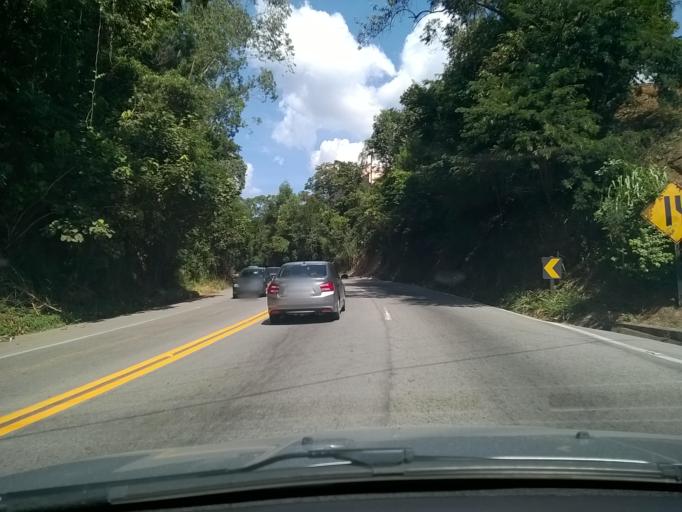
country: BR
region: Sao Paulo
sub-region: Jundiai
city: Jundiai
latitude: -23.2236
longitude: -46.8689
